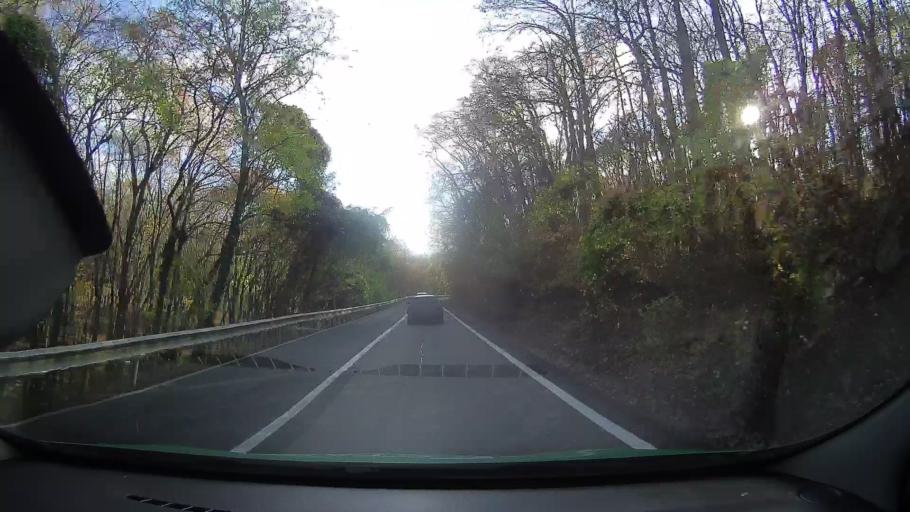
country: RO
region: Tulcea
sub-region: Comuna Topolog
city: Topolog
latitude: 44.9127
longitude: 28.4193
